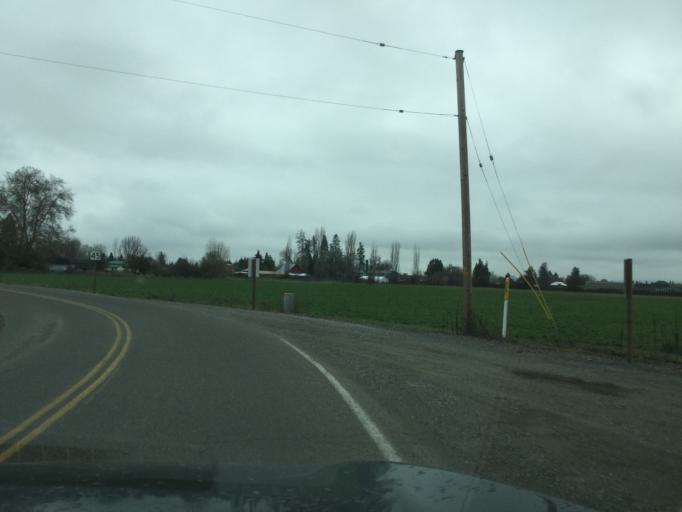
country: US
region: Oregon
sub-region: Jackson County
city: Central Point
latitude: 42.3896
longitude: -122.9411
